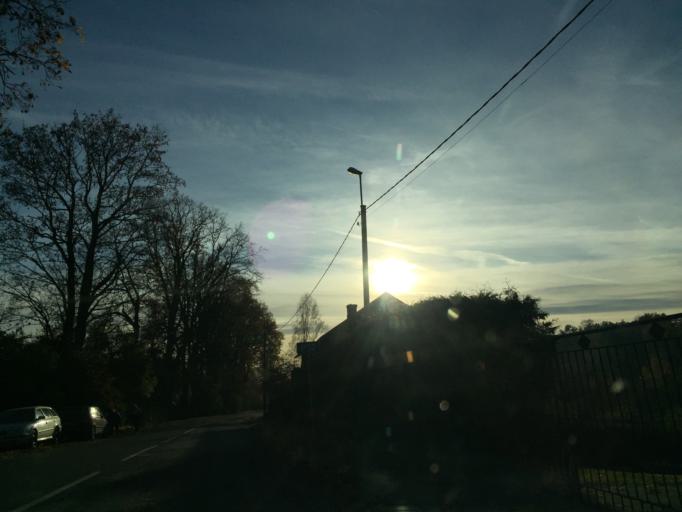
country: LV
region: Skriveri
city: Skriveri
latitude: 56.6409
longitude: 25.1147
